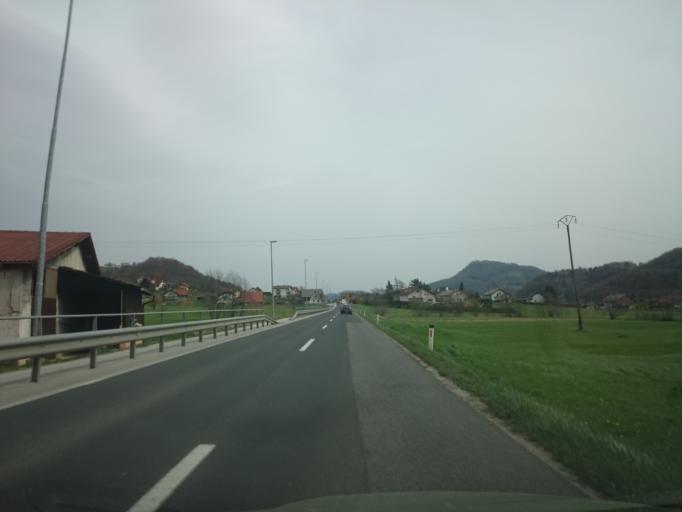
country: SI
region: Sentjur pri Celju
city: Sentjur
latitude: 46.2177
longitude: 15.3635
